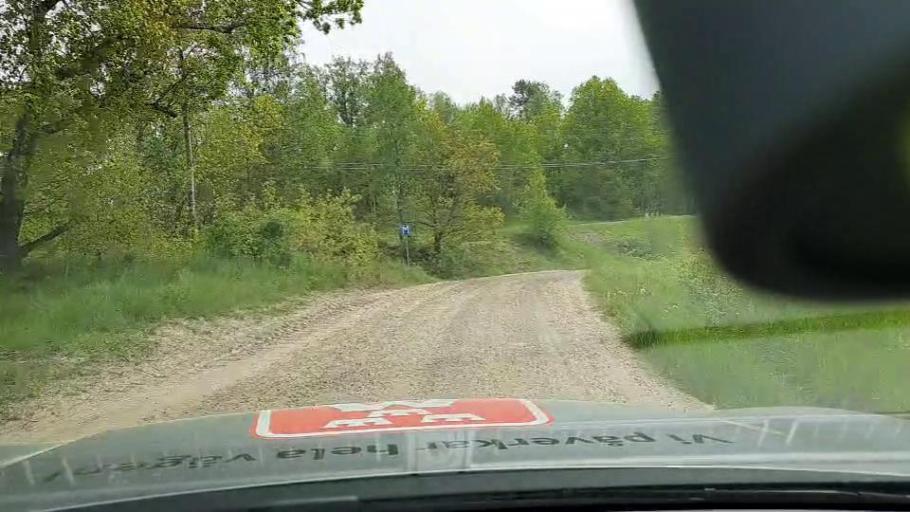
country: SE
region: Soedermanland
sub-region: Flens Kommun
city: Flen
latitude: 59.0404
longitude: 16.5801
